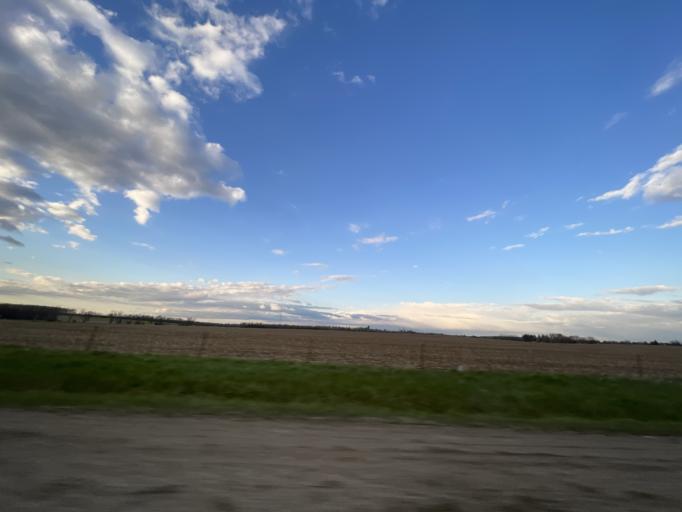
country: CA
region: Ontario
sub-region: Wellington County
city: Guelph
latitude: 43.5836
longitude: -80.2952
